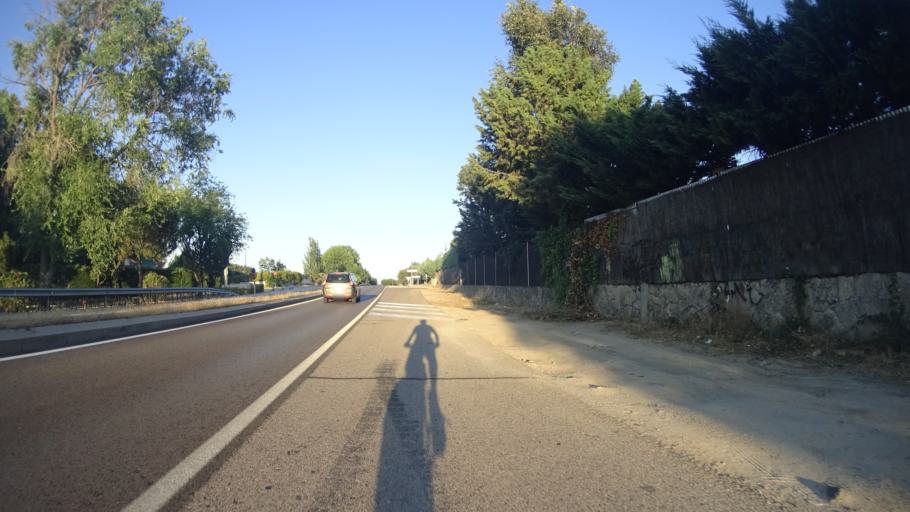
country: ES
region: Madrid
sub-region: Provincia de Madrid
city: Galapagar
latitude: 40.5701
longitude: -3.9884
